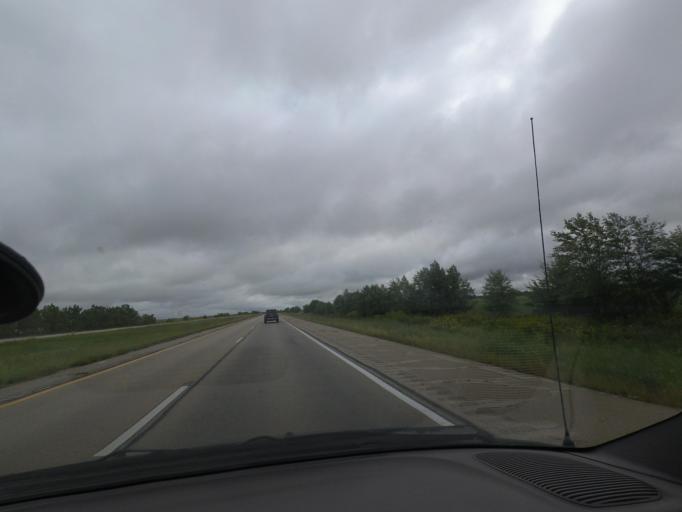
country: US
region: Illinois
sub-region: Piatt County
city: Monticello
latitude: 40.0238
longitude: -88.6867
